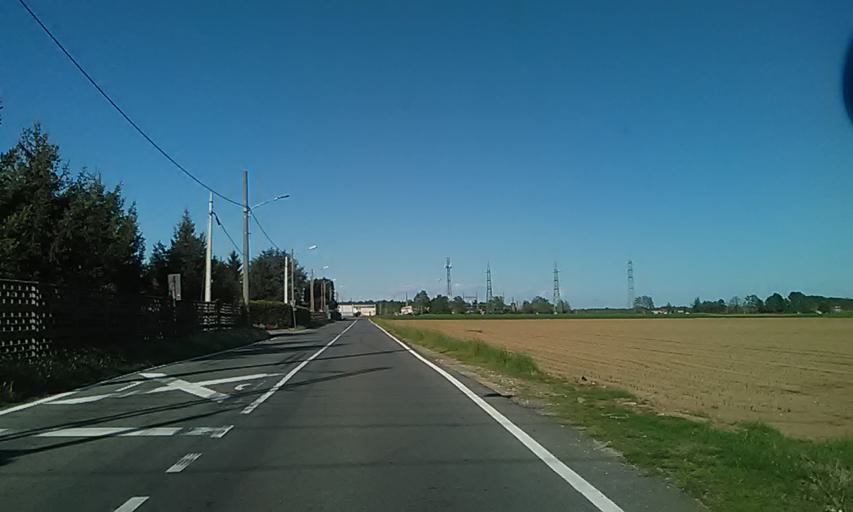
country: IT
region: Piedmont
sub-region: Provincia di Novara
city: Momo
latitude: 45.5779
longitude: 8.5543
